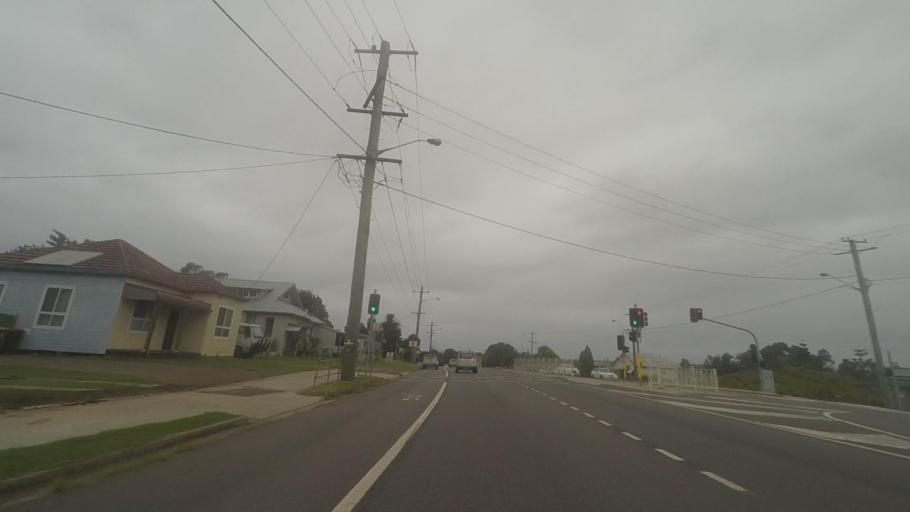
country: AU
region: New South Wales
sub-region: Newcastle
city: Mayfield West
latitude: -32.8635
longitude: 151.7056
